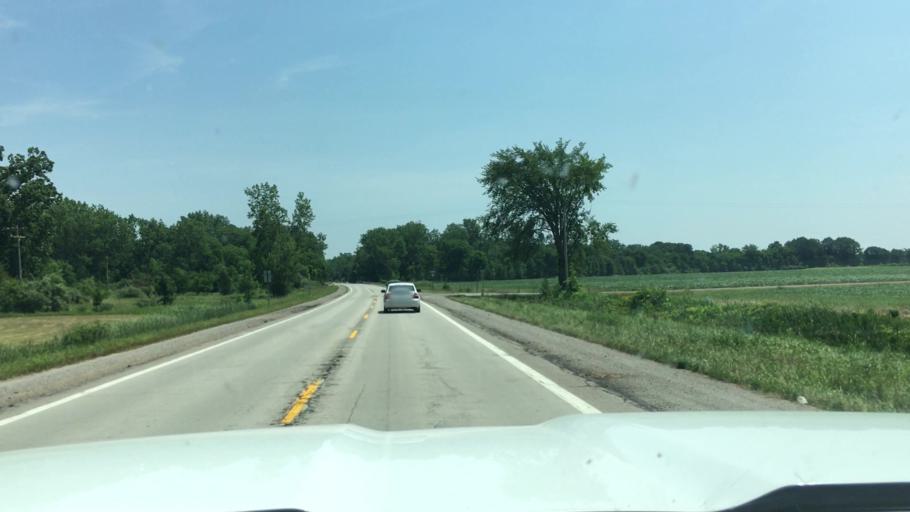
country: US
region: Michigan
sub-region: Shiawassee County
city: New Haven
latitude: 43.1864
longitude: -84.2878
